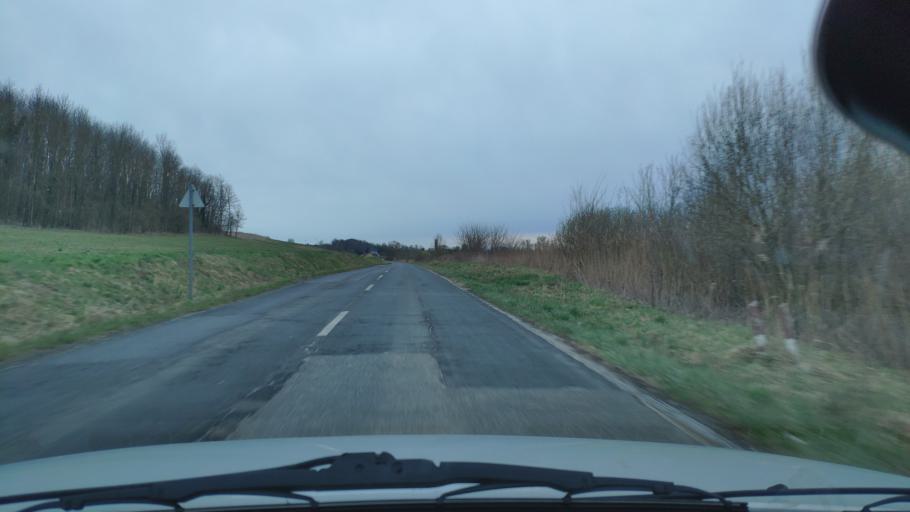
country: HU
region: Zala
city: Nagykanizsa
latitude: 46.5264
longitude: 16.9822
